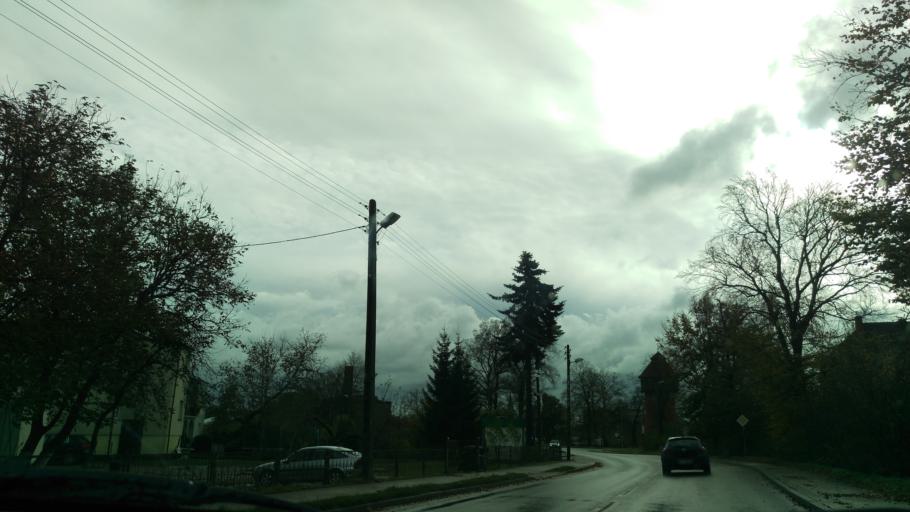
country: PL
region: West Pomeranian Voivodeship
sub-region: Powiat gryficki
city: Ploty
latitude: 53.8092
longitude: 15.2615
